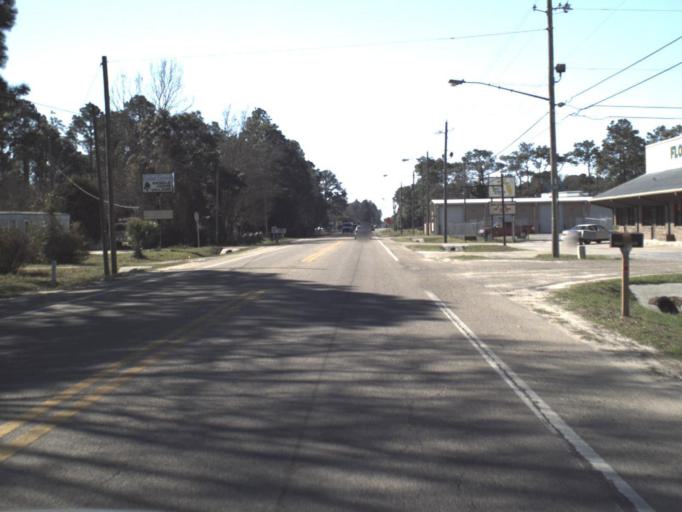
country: US
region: Florida
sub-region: Bay County
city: Cedar Grove
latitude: 30.1818
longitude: -85.6249
